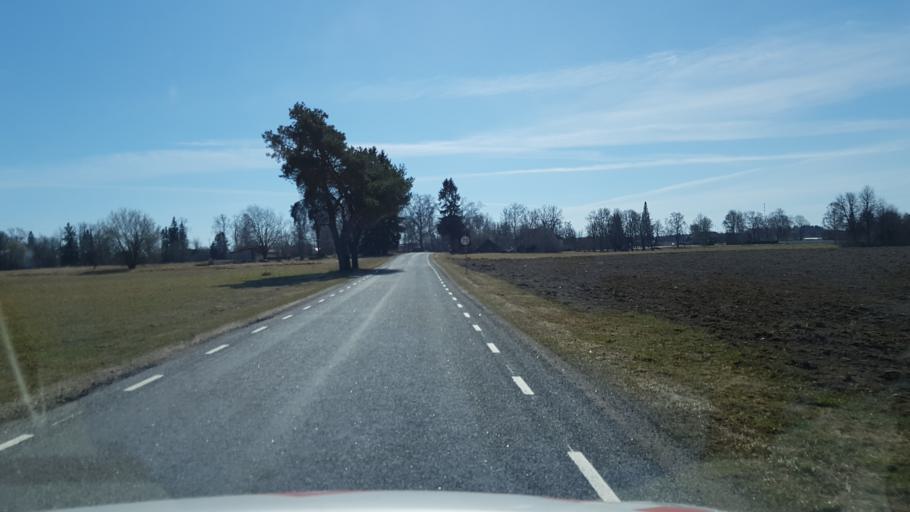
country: EE
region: Laeaene-Virumaa
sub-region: Vinni vald
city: Vinni
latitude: 59.1020
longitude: 26.5262
